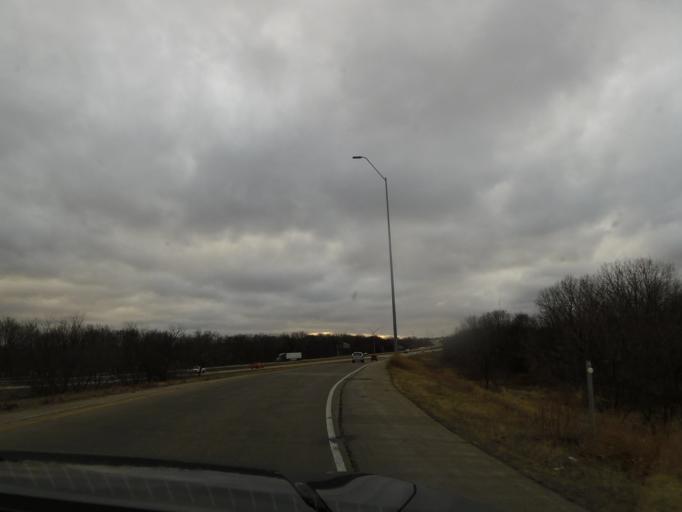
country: US
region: Iowa
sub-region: Black Hawk County
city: Evansdale
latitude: 42.4598
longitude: -92.2980
